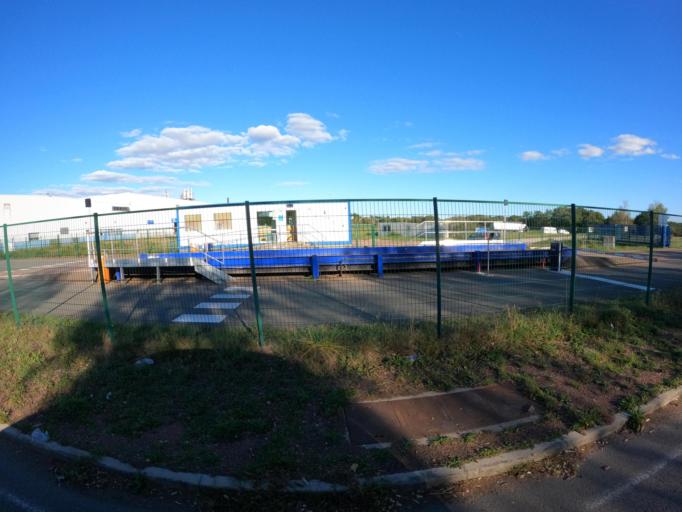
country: FR
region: Bourgogne
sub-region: Departement de Saone-et-Loire
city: Torcy
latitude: 46.7560
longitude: 4.4409
